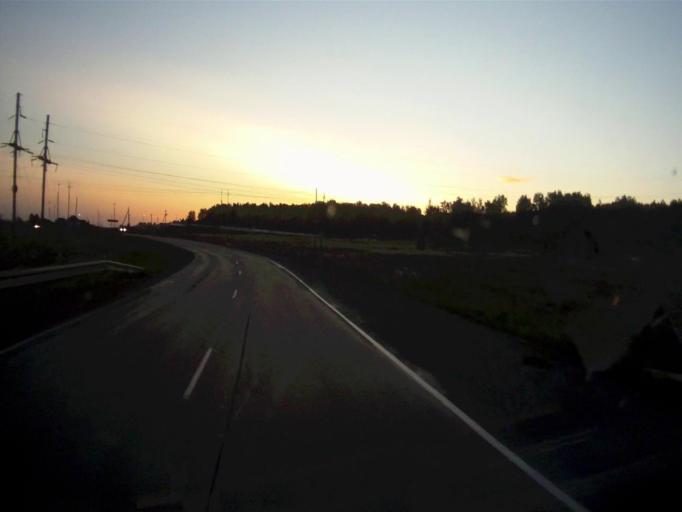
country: RU
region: Chelyabinsk
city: Poletayevo
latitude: 55.2251
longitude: 60.9969
